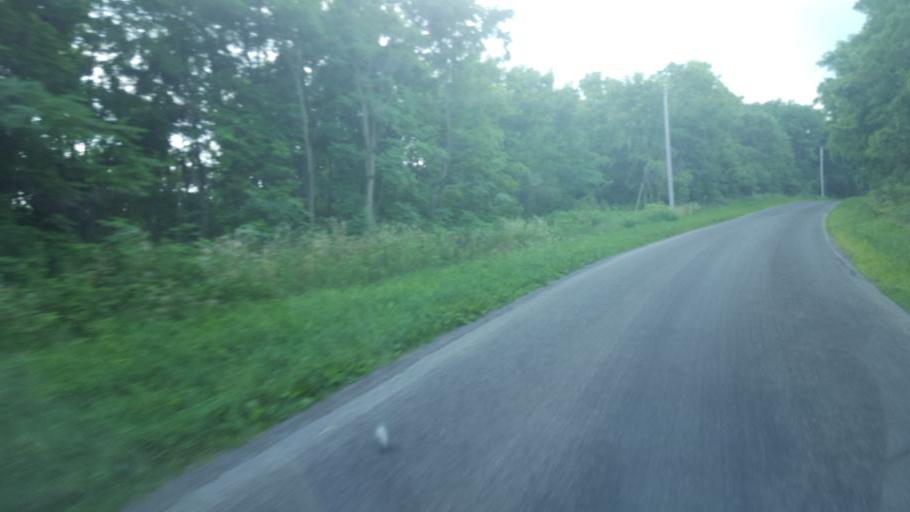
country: US
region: Ohio
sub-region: Hardin County
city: Kenton
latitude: 40.5850
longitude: -83.5703
